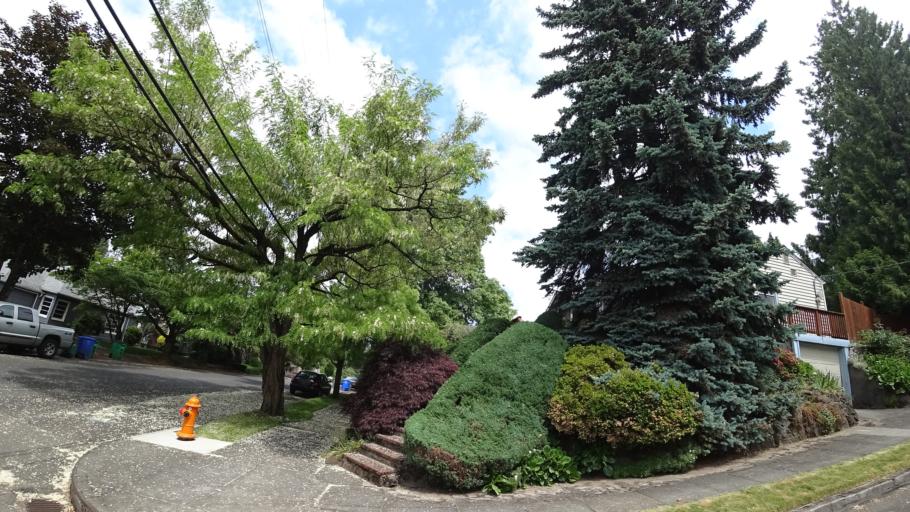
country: US
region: Oregon
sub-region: Clackamas County
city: Lake Oswego
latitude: 45.4669
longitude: -122.6899
